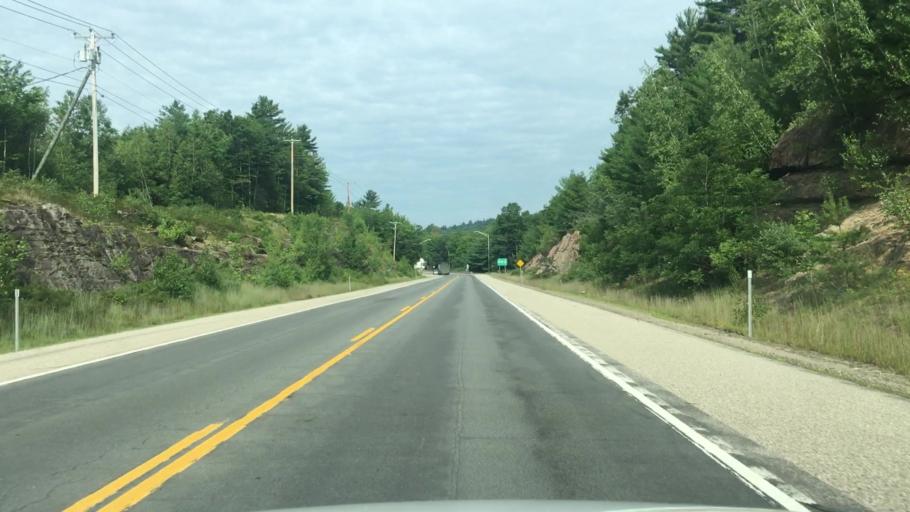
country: US
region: New Hampshire
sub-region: Carroll County
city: Tamworth
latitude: 43.8297
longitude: -71.2699
